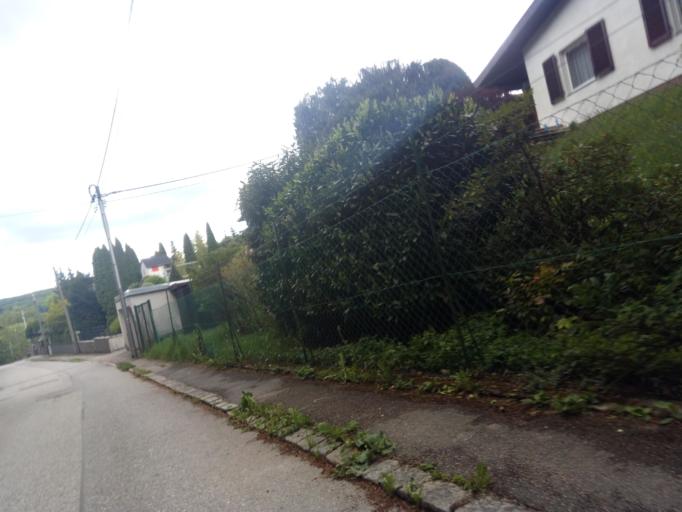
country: AT
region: Lower Austria
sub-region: Politischer Bezirk Modling
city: Breitenfurt bei Wien
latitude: 48.1427
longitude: 16.1460
